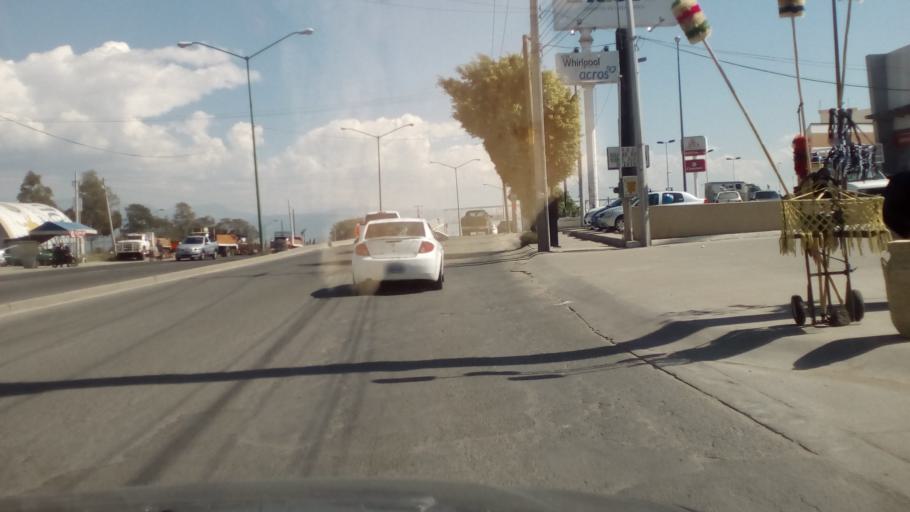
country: MX
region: Guanajuato
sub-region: Leon
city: Ejido la Joya
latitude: 21.1354
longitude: -101.7200
